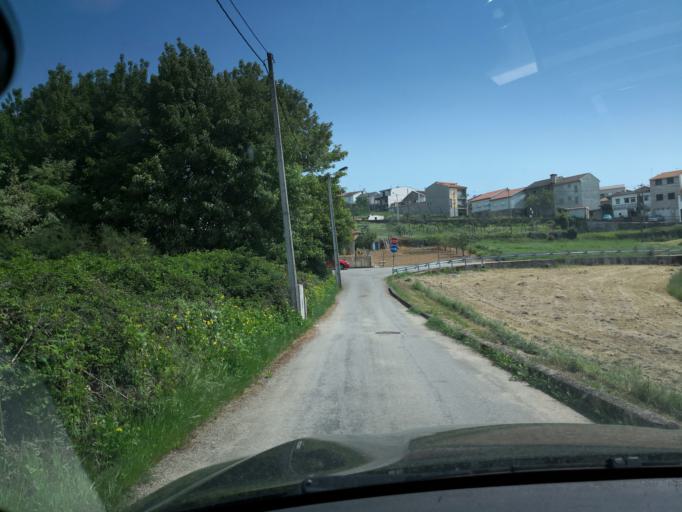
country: PT
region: Vila Real
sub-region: Vila Real
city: Vila Real
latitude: 41.2898
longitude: -7.7164
